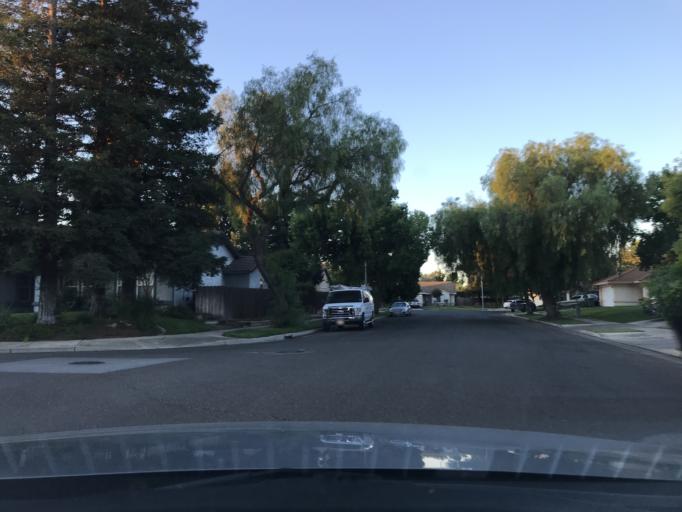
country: US
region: California
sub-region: Merced County
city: Merced
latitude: 37.3114
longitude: -120.5012
